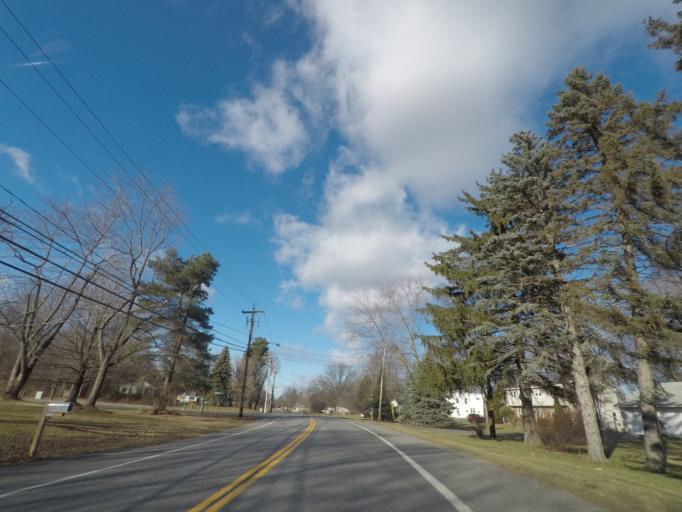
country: US
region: New York
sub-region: Saratoga County
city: Waterford
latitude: 42.8346
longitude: -73.7289
